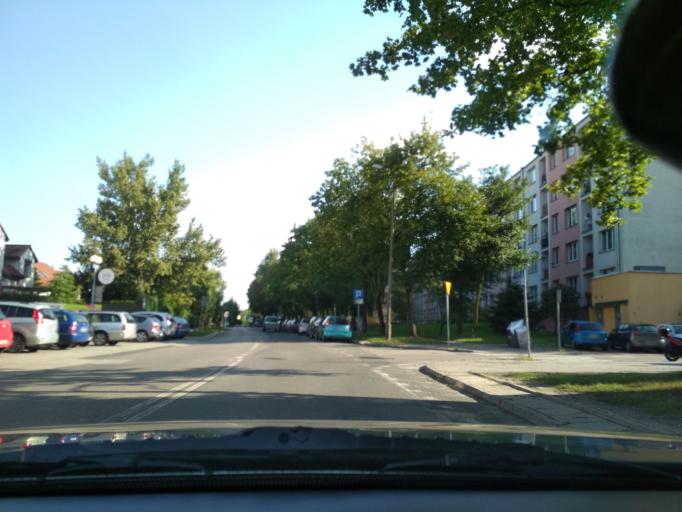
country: PL
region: Silesian Voivodeship
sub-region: Gliwice
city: Gliwice
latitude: 50.2765
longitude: 18.6578
